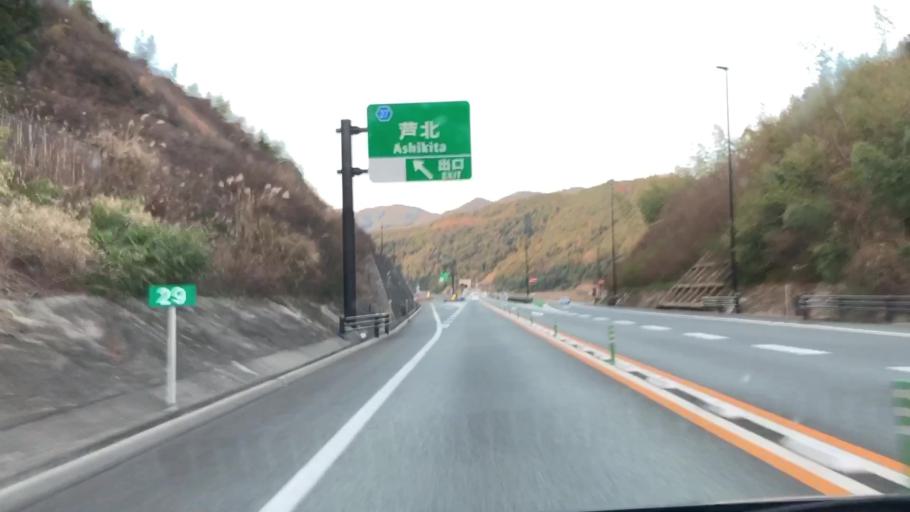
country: JP
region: Kumamoto
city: Minamata
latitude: 32.2953
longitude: 130.5079
